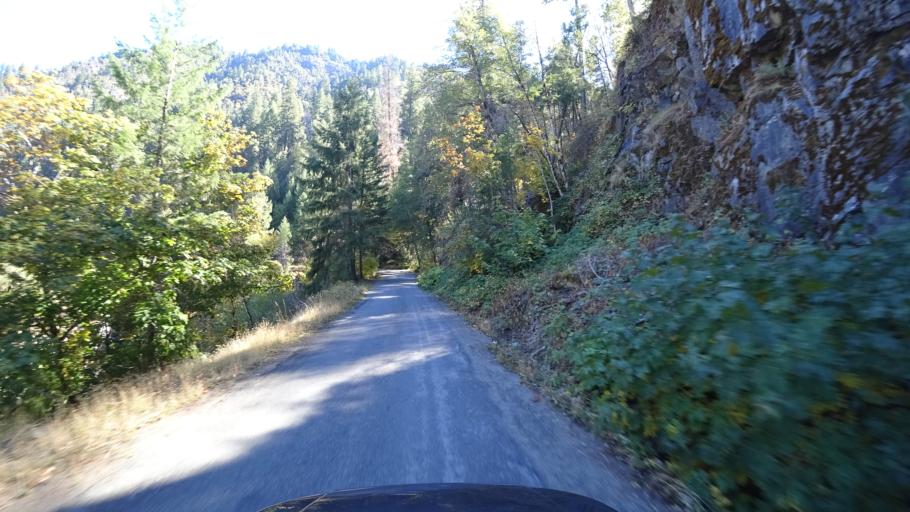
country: US
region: California
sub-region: Siskiyou County
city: Happy Camp
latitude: 41.3358
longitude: -123.3960
